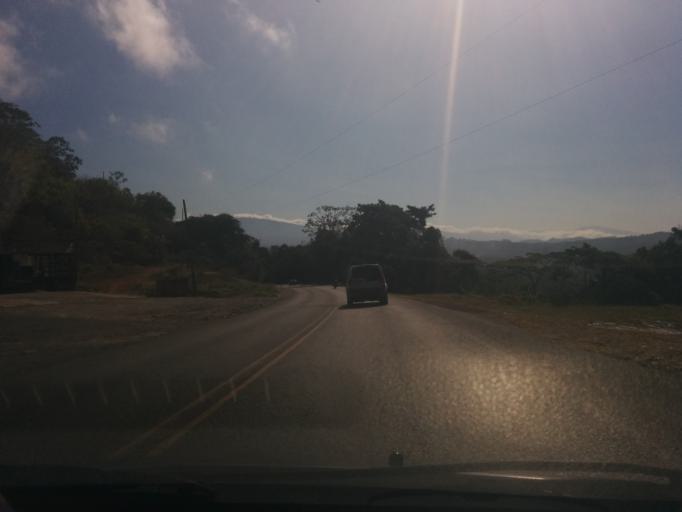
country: CR
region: Alajuela
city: San Rafael
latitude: 10.0686
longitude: -84.4958
